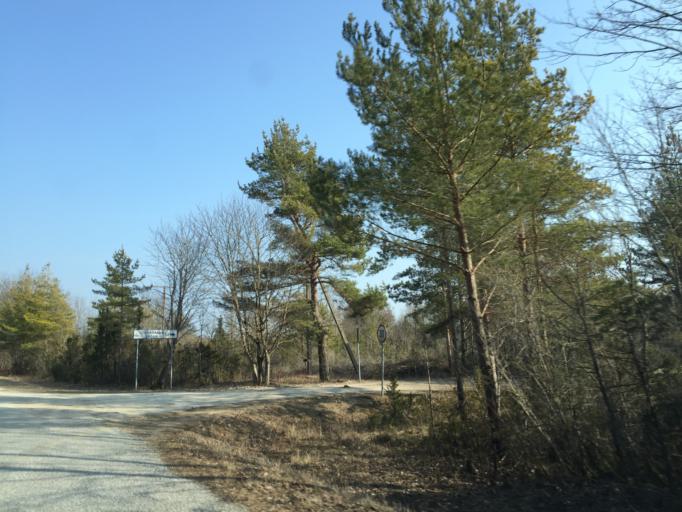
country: EE
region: Saare
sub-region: Orissaare vald
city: Orissaare
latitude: 58.5537
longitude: 23.3096
